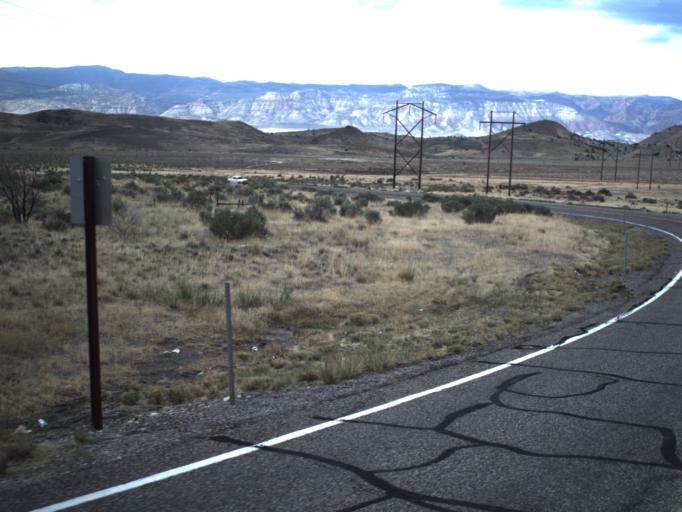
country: US
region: Utah
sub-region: Sevier County
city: Richfield
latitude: 38.7748
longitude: -111.9505
